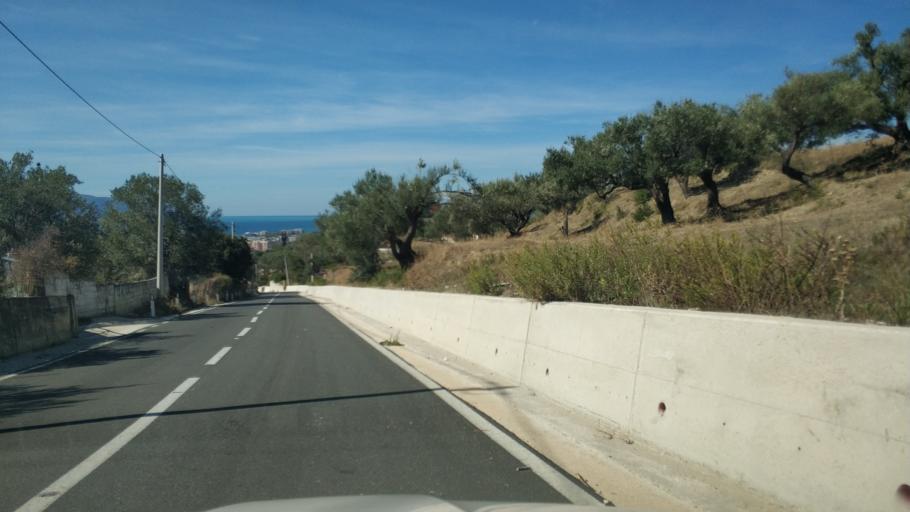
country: AL
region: Vlore
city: Vlore
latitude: 40.4576
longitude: 19.5088
